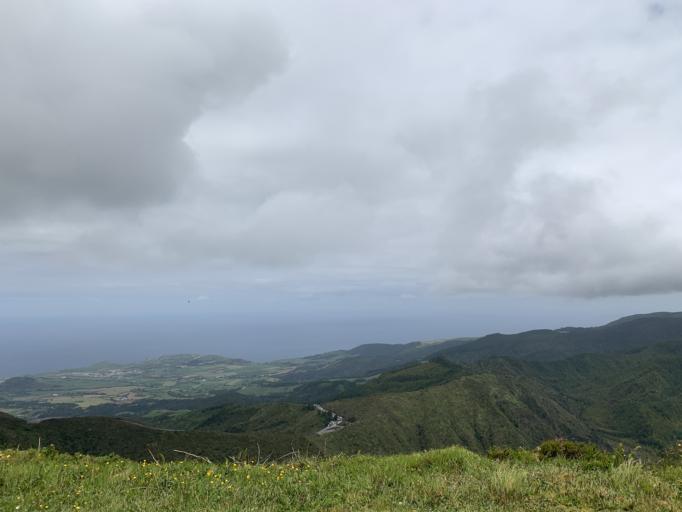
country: PT
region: Azores
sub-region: Vila Franca do Campo
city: Vila Franca do Campo
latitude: 37.7607
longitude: -25.4919
